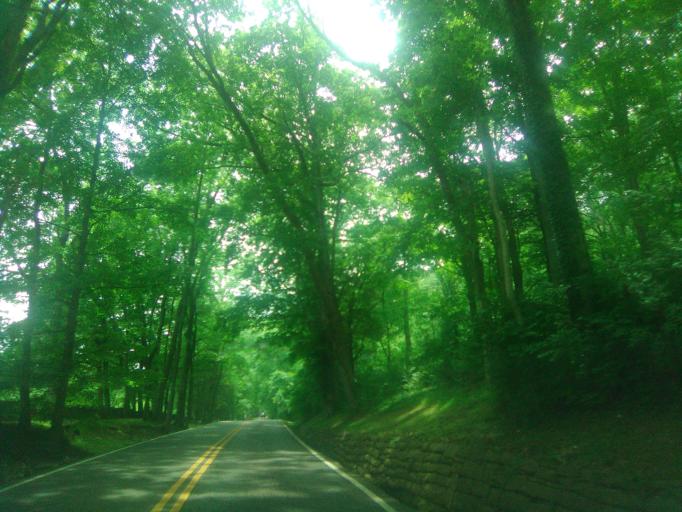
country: US
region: Tennessee
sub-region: Davidson County
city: Belle Meade
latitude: 36.0805
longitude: -86.8673
